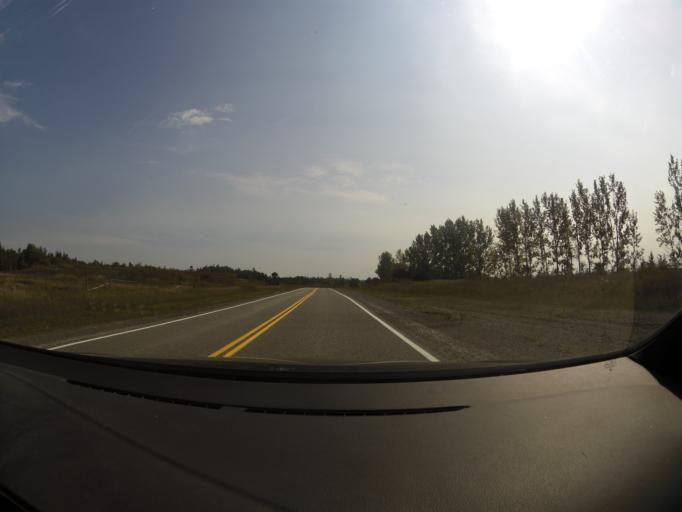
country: CA
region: Ontario
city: Arnprior
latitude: 45.3409
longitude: -76.1943
